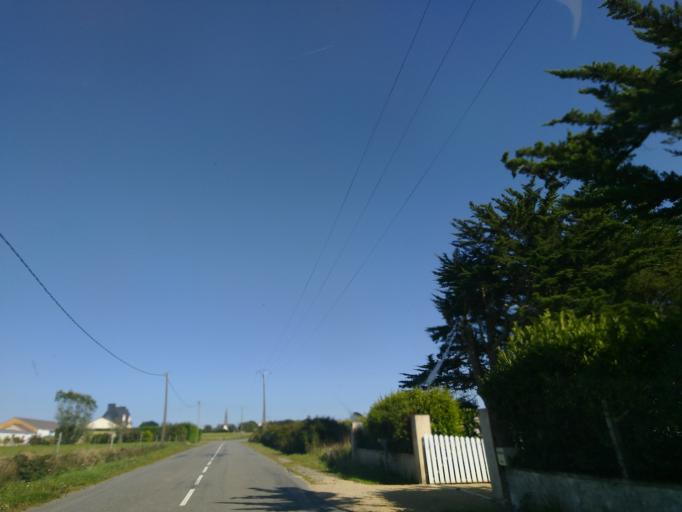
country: FR
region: Brittany
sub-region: Departement du Finistere
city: Le Faou
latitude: 48.2638
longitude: -4.2036
